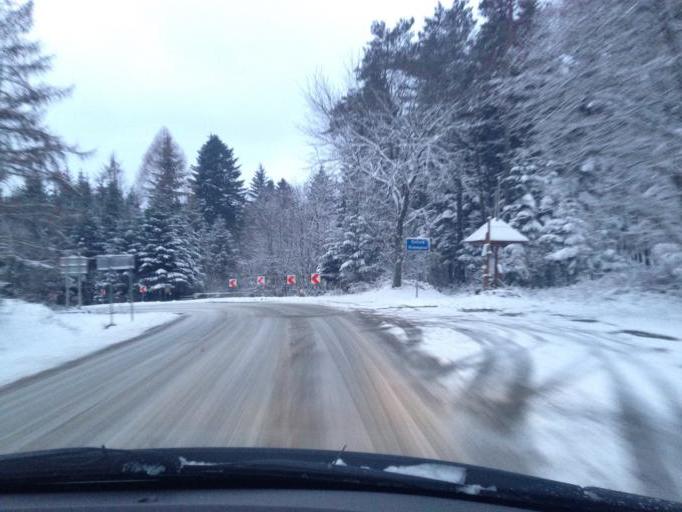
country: PL
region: Subcarpathian Voivodeship
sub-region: Powiat jasielski
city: Krempna
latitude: 49.5335
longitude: 21.4986
